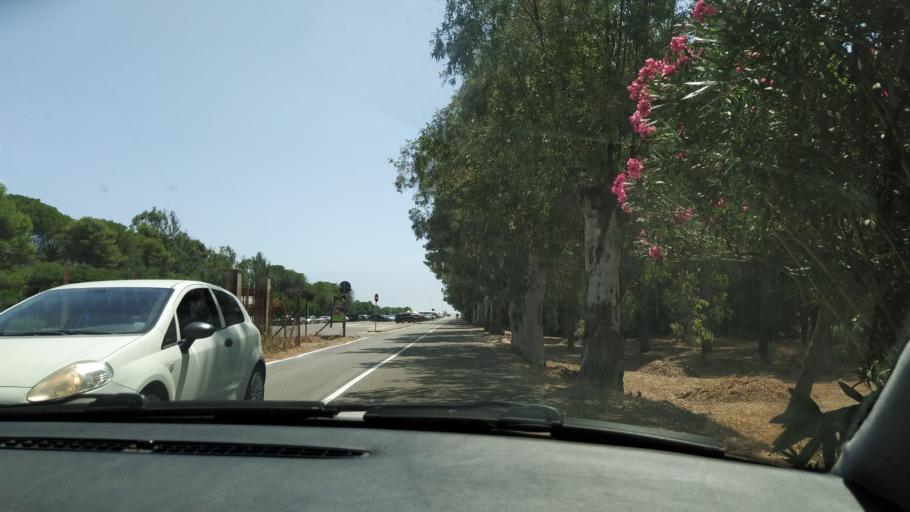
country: IT
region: Basilicate
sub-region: Provincia di Matera
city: Marconia
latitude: 40.3221
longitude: 16.7966
